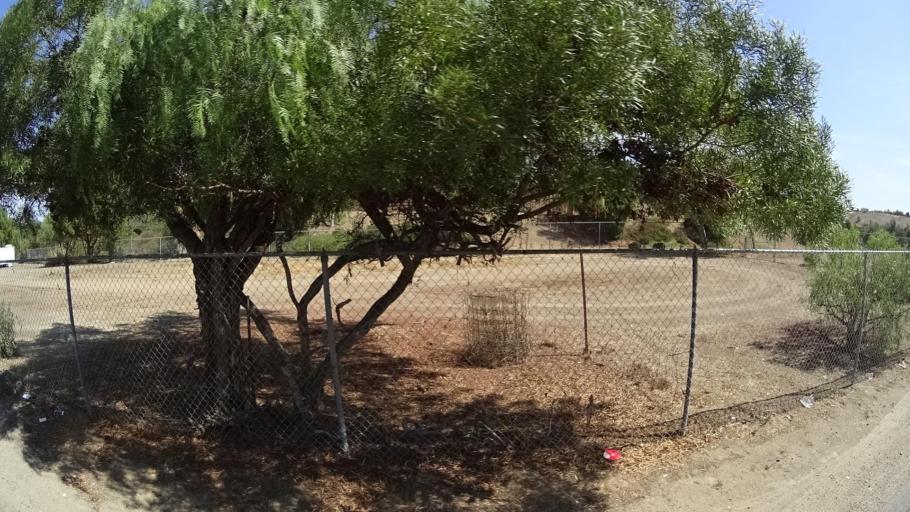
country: US
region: California
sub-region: San Diego County
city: La Presa
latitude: 32.6728
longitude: -116.9974
